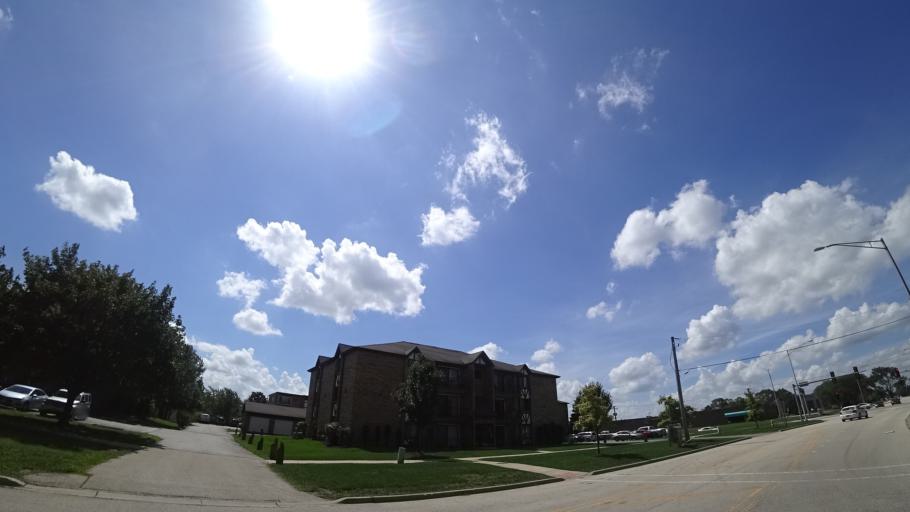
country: US
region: Illinois
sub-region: Cook County
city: Tinley Park
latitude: 41.5732
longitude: -87.7920
